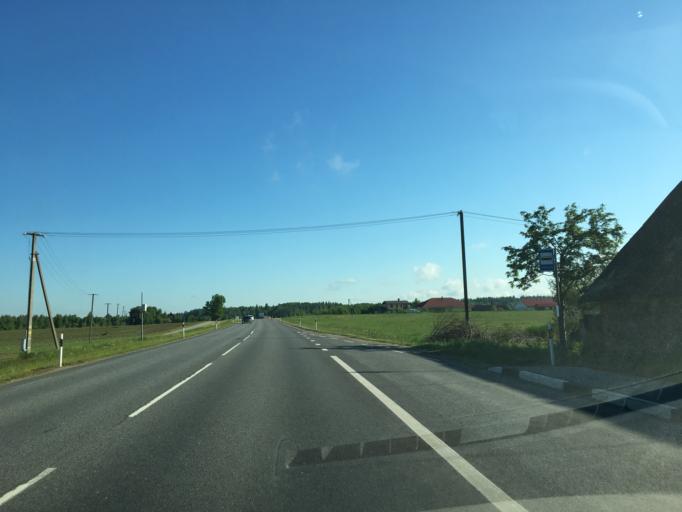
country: EE
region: Tartu
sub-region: Tartu linn
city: Tartu
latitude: 58.4373
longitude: 26.6811
